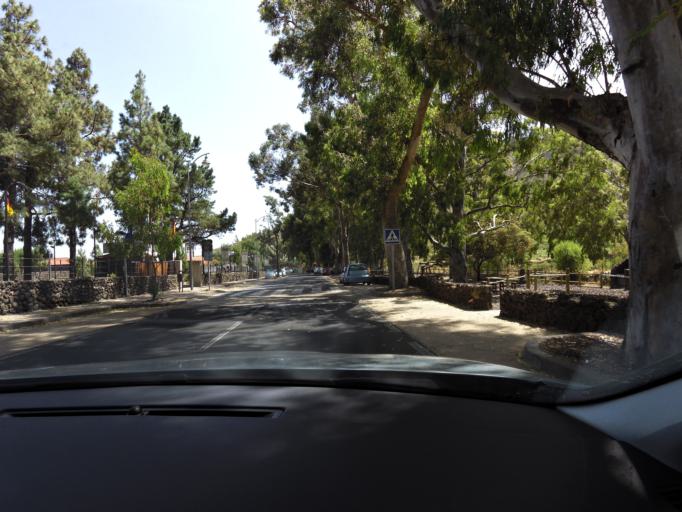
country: ES
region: Canary Islands
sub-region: Provincia de Santa Cruz de Tenerife
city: Santiago del Teide
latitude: 28.2988
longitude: -16.8160
